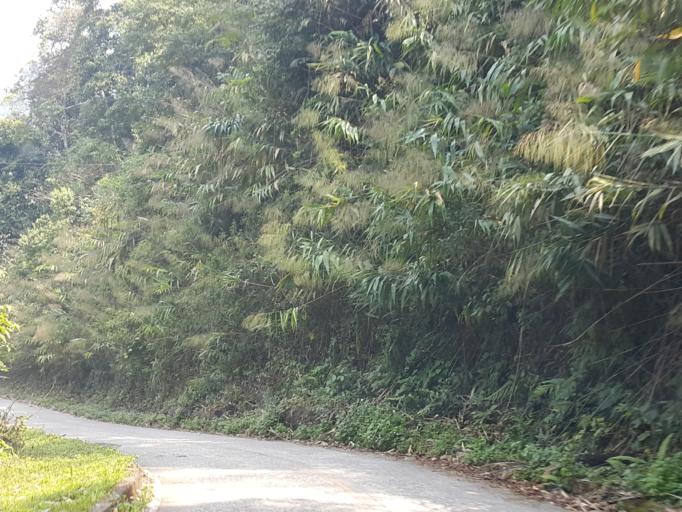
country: TH
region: Lampang
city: Mueang Pan
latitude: 18.8285
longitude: 99.4206
